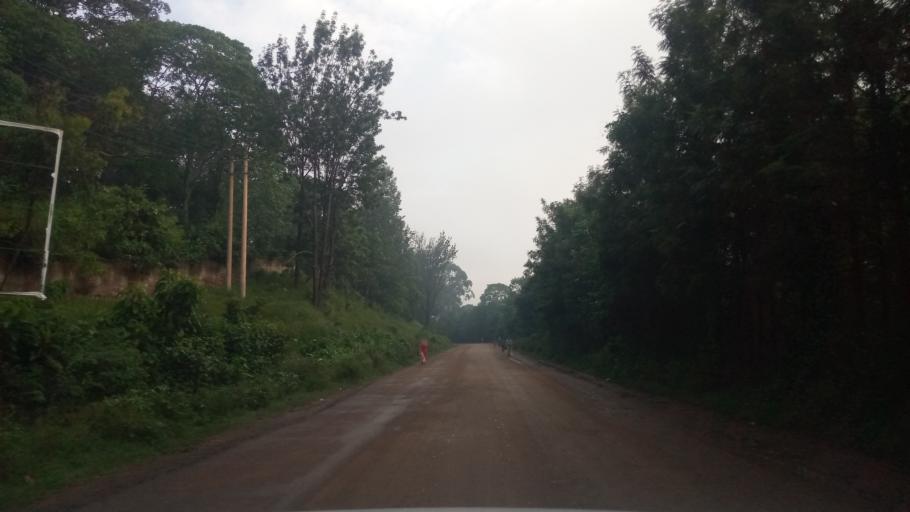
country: ET
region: Oromiya
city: Jima
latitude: 7.6835
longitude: 36.8331
